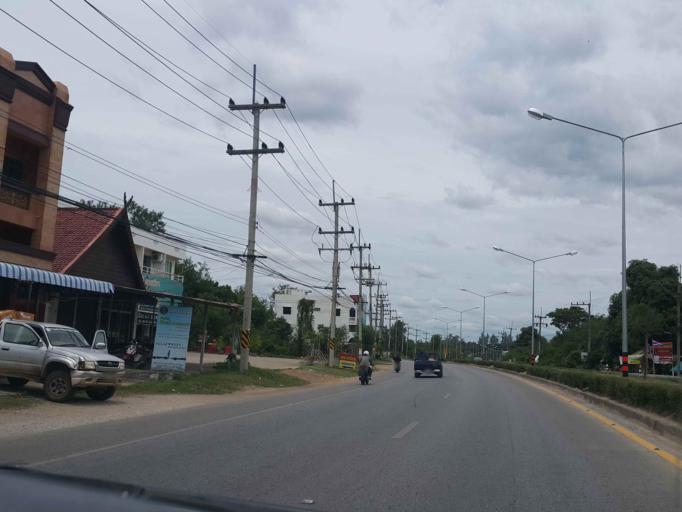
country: TH
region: Chiang Mai
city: San Pa Tong
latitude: 18.5786
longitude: 98.8814
